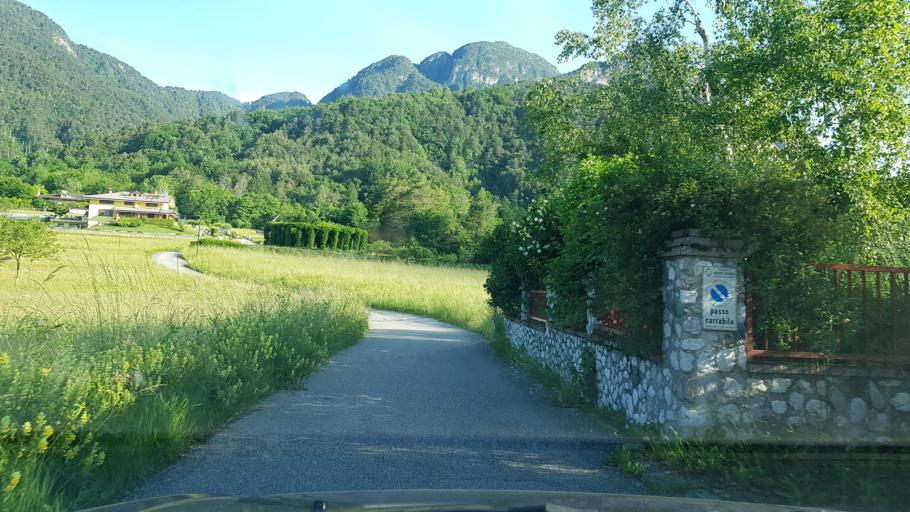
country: IT
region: Friuli Venezia Giulia
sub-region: Provincia di Udine
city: Moggio di Sotto
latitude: 46.4082
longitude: 13.1922
